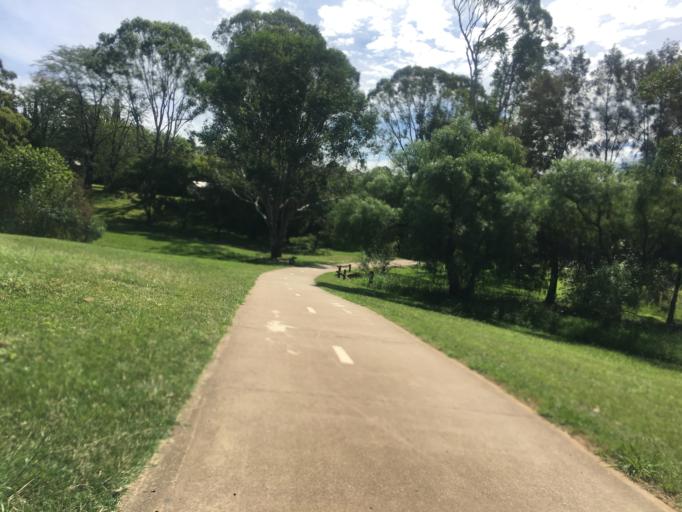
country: AU
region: New South Wales
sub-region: Camden
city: Camden South
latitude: -34.0799
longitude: 150.6996
